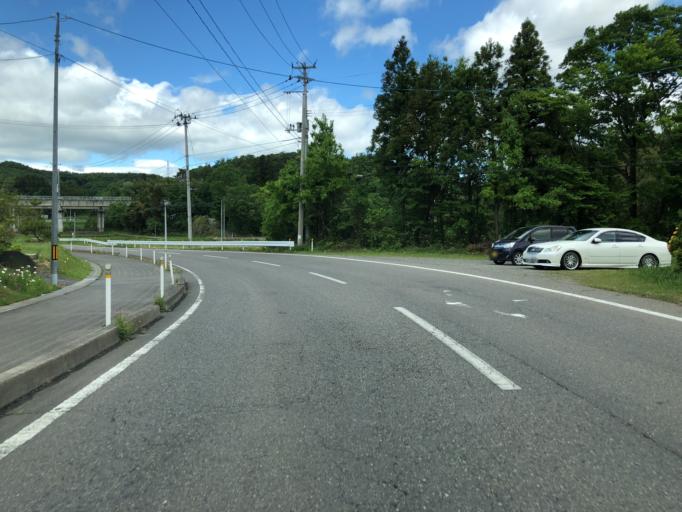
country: JP
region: Fukushima
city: Motomiya
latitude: 37.4950
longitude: 140.4266
